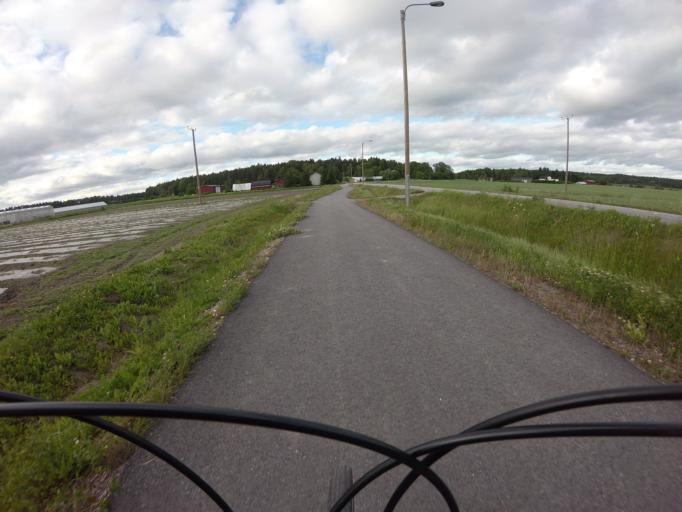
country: FI
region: Varsinais-Suomi
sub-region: Turku
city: Turku
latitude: 60.5092
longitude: 22.3389
